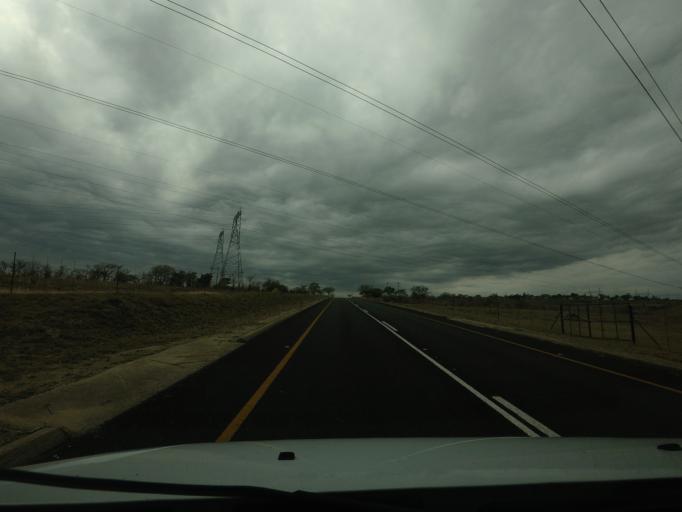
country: ZA
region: Limpopo
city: Thulamahashi
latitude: -24.5643
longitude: 31.0523
